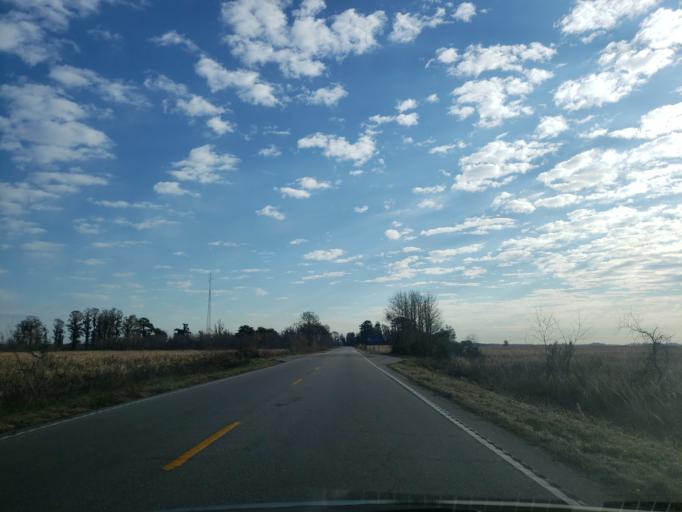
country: US
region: Georgia
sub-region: Chatham County
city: Port Wentworth
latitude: 32.1660
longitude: -81.1212
